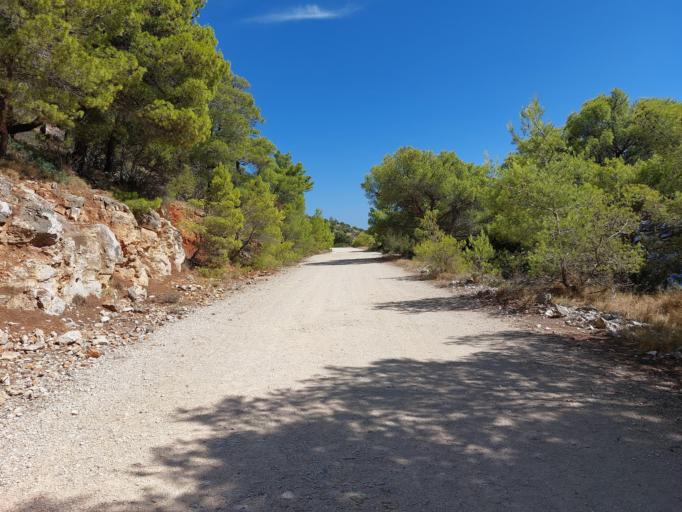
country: HR
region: Dubrovacko-Neretvanska
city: Smokvica
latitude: 42.7355
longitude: 16.8339
